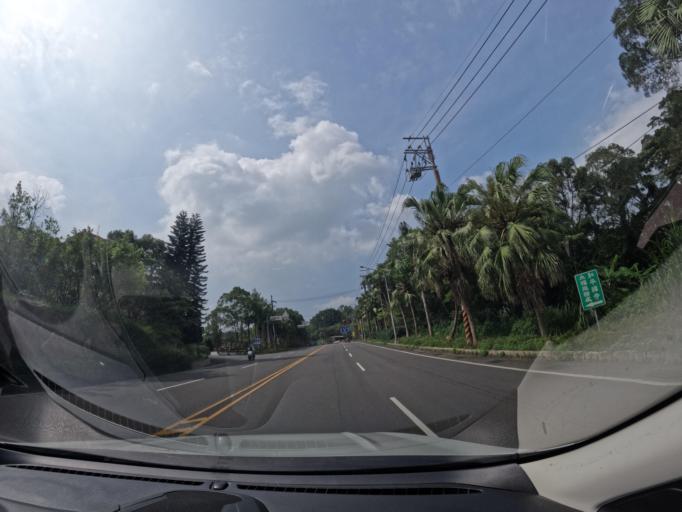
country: TW
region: Taiwan
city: Daxi
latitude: 24.8947
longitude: 121.3329
